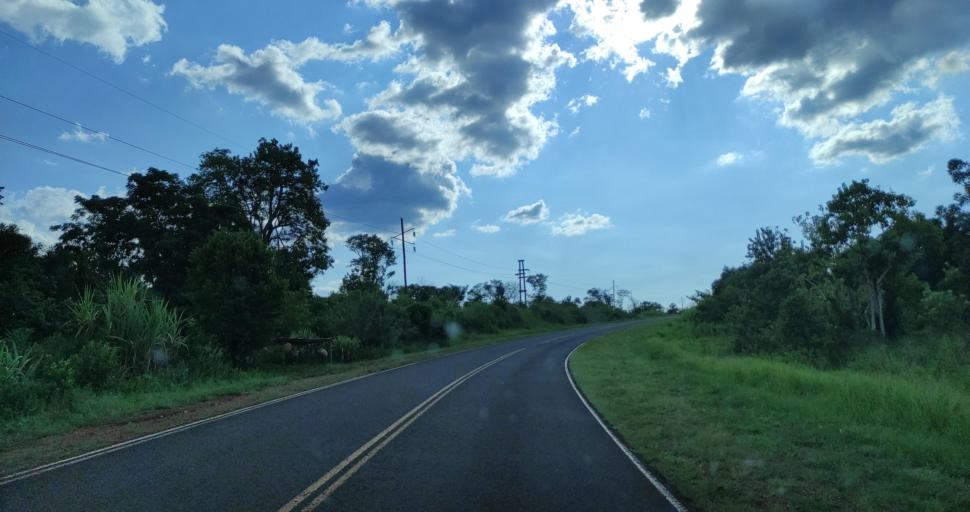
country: AR
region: Misiones
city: San Vicente
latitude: -26.3511
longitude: -54.1877
